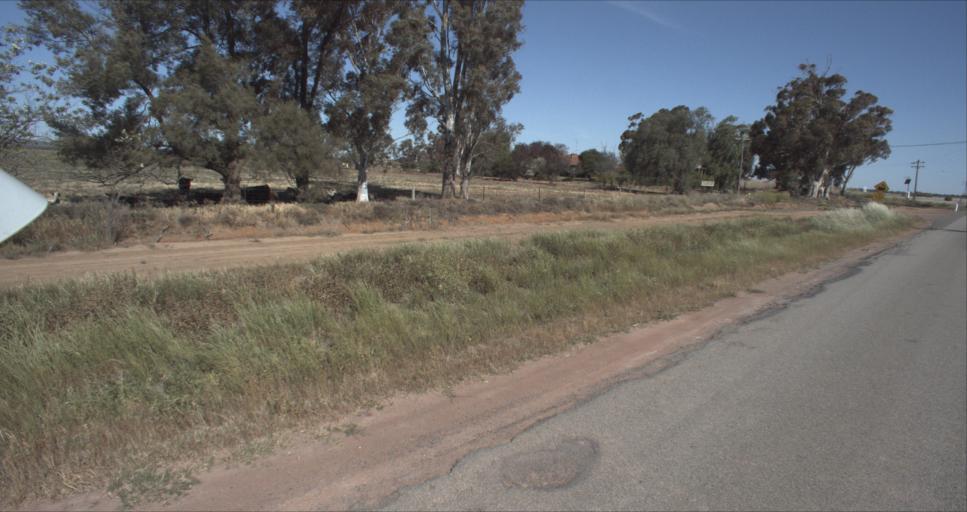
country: AU
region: New South Wales
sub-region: Leeton
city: Leeton
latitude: -34.4769
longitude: 146.3681
